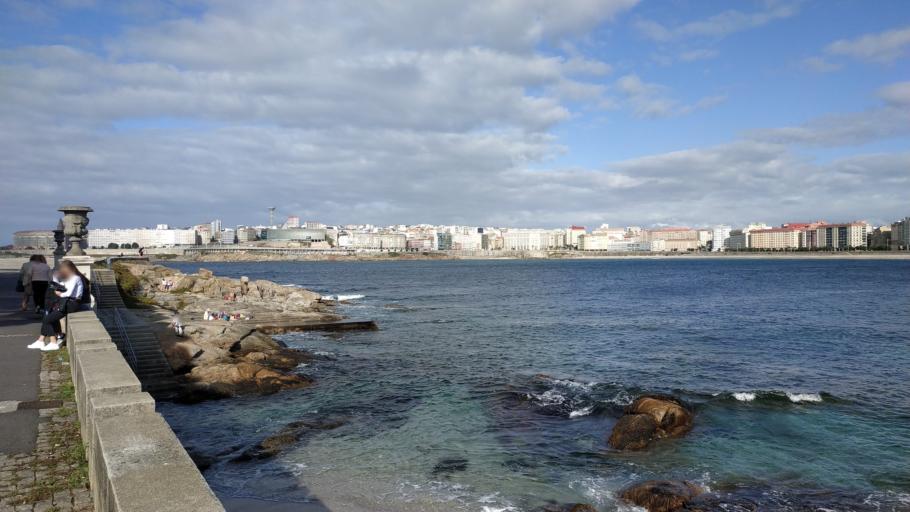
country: ES
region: Galicia
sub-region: Provincia da Coruna
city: A Coruna
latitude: 43.3699
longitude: -8.4146
